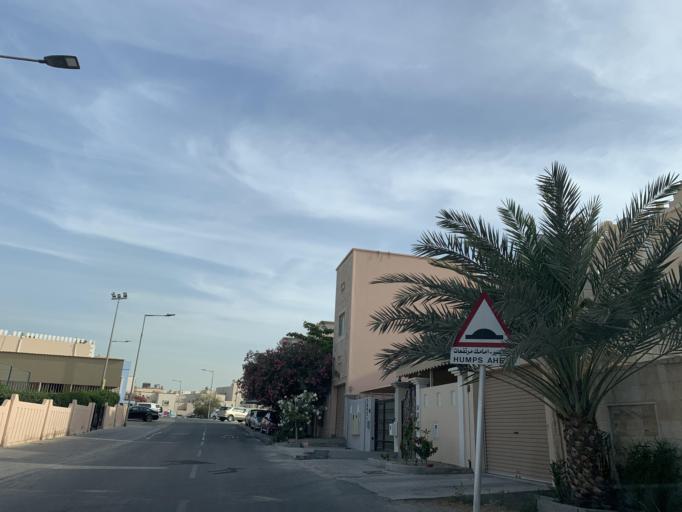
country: BH
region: Northern
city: Ar Rifa'
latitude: 26.1251
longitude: 50.5824
